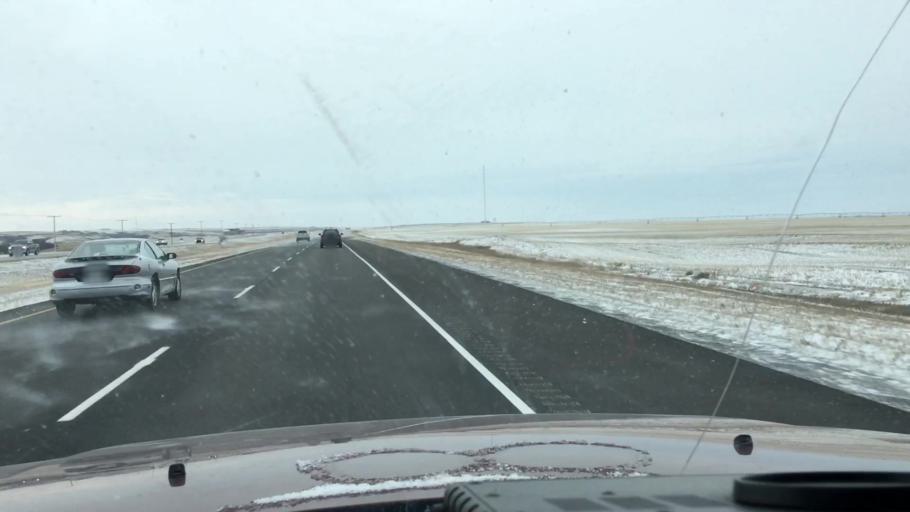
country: CA
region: Saskatchewan
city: Saskatoon
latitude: 51.7506
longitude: -106.4764
